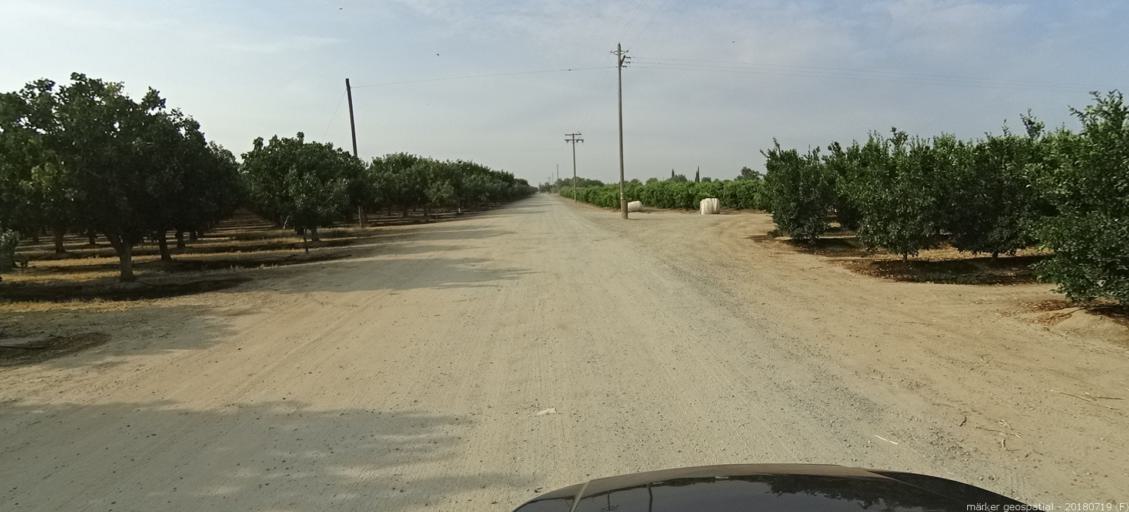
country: US
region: California
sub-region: Madera County
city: Fairmead
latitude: 37.1026
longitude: -120.1931
